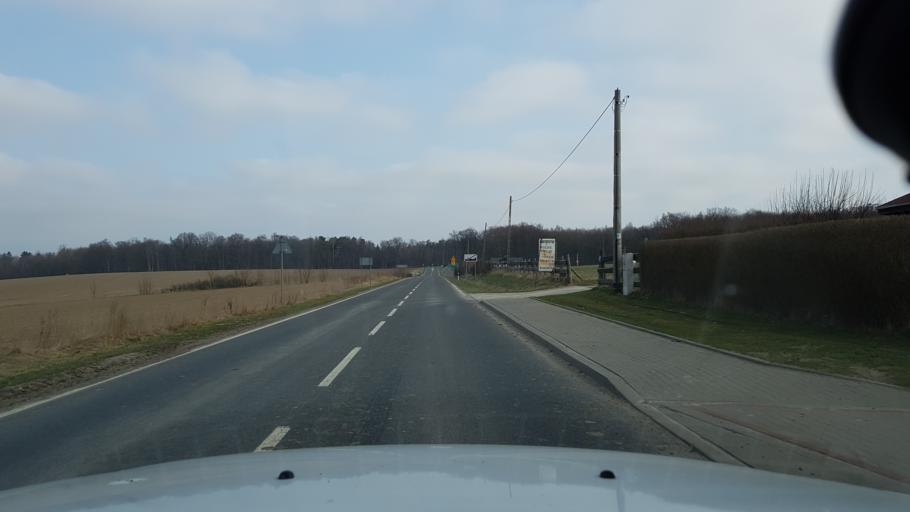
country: PL
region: West Pomeranian Voivodeship
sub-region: Powiat koszalinski
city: Sianow
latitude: 54.2675
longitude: 16.2678
